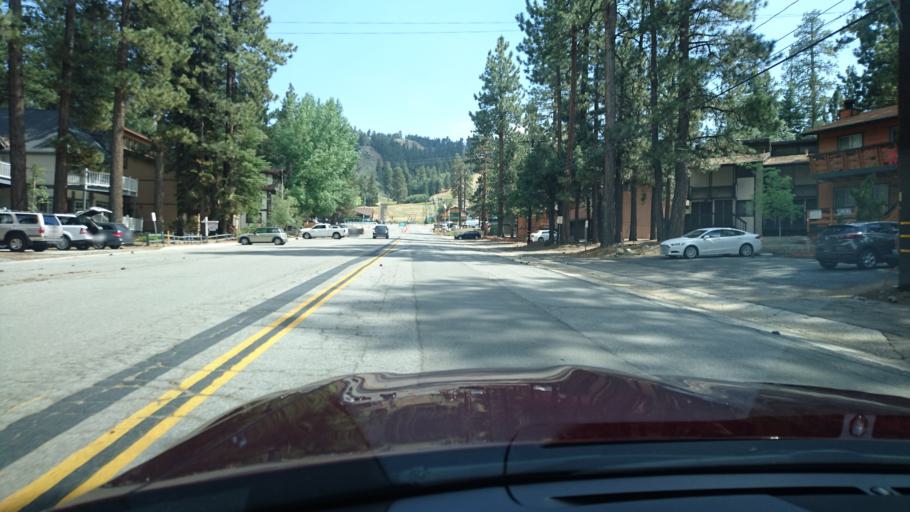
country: US
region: California
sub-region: San Bernardino County
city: Big Bear Lake
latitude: 34.2385
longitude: -116.8885
